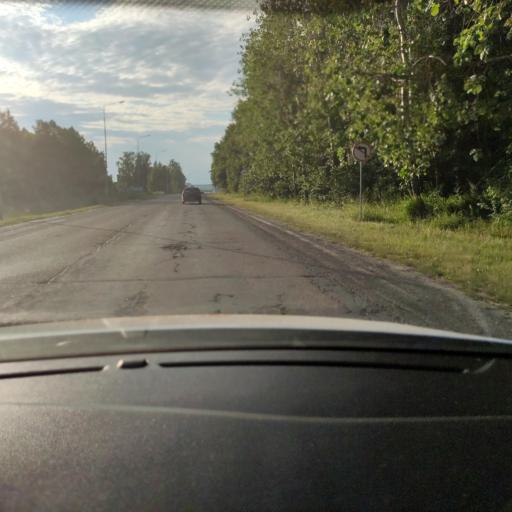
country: RU
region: Tatarstan
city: Vysokaya Gora
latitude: 55.9736
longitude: 49.3125
